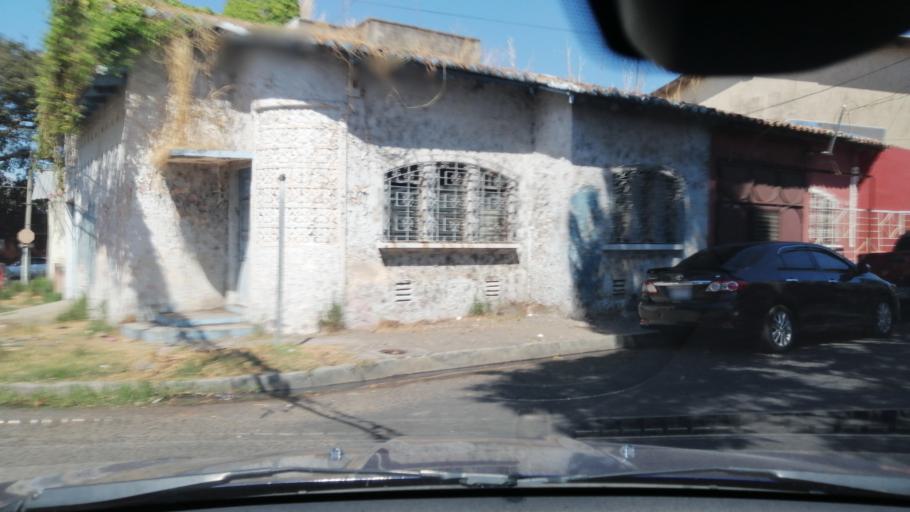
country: SV
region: Santa Ana
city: Santa Ana
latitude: 13.9961
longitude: -89.5650
